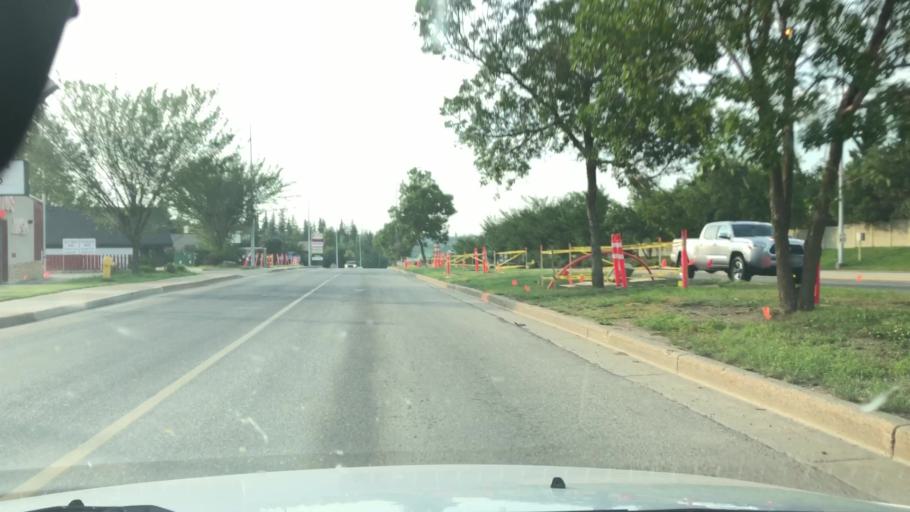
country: CA
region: Alberta
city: St. Albert
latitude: 53.6281
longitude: -113.6198
